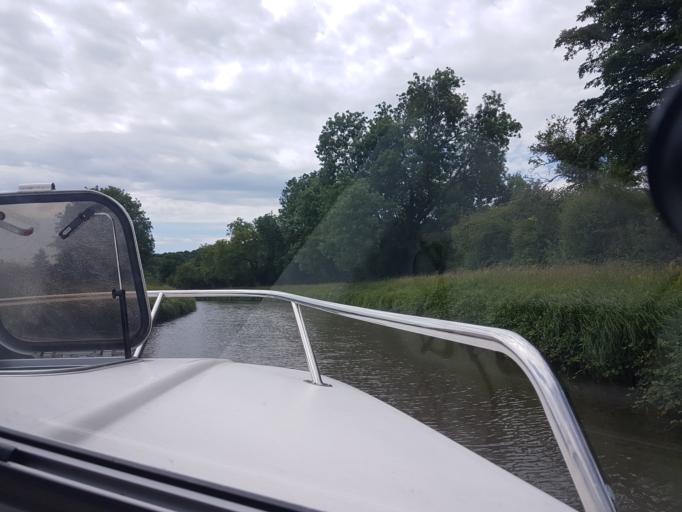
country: FR
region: Bourgogne
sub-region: Departement de la Nievre
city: Clamecy
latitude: 47.4953
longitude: 3.5102
